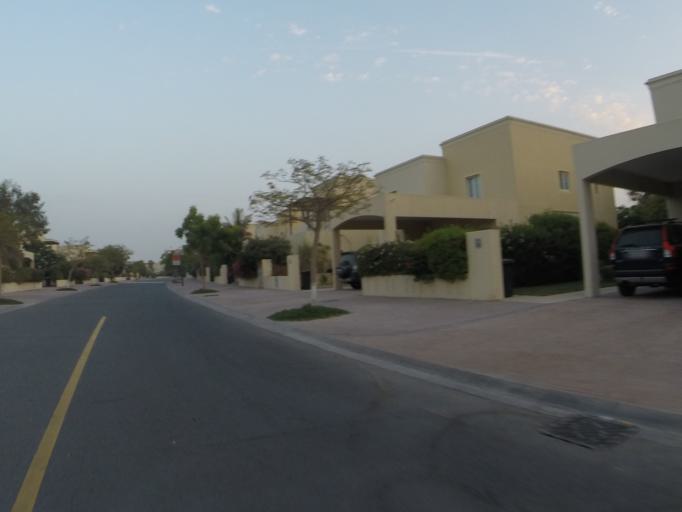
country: AE
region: Dubai
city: Dubai
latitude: 25.0729
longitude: 55.1525
